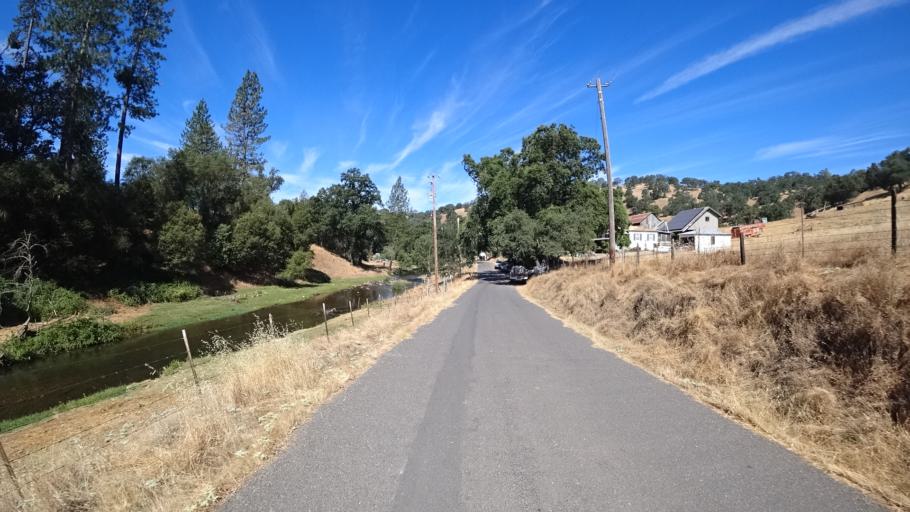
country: US
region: California
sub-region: Calaveras County
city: Mountain Ranch
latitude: 38.1480
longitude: -120.5835
